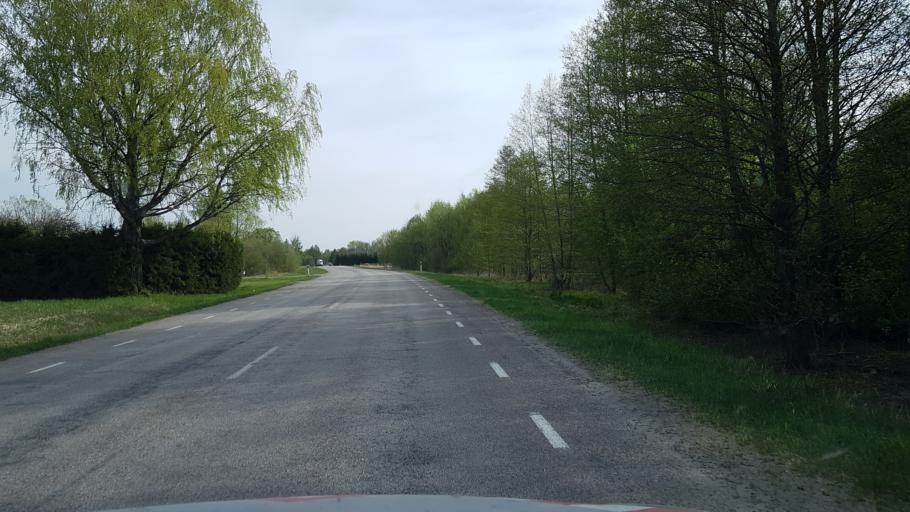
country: EE
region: Paernumaa
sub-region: Audru vald
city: Audru
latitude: 58.4001
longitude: 24.2972
